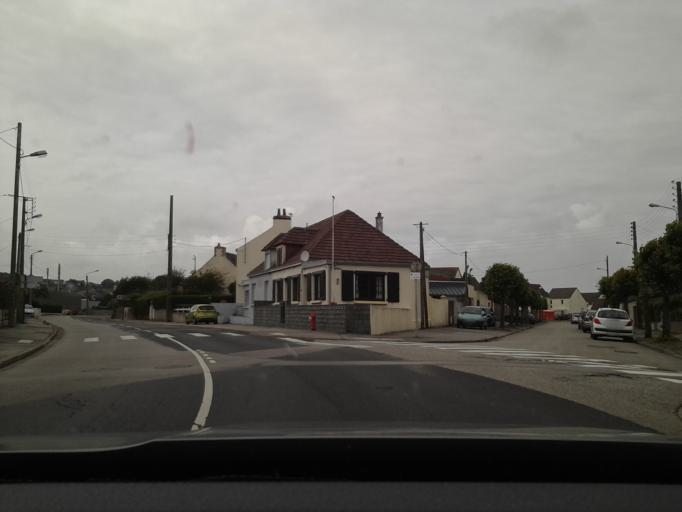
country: FR
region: Lower Normandy
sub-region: Departement de la Manche
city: Querqueville
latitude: 49.6618
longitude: -1.6817
